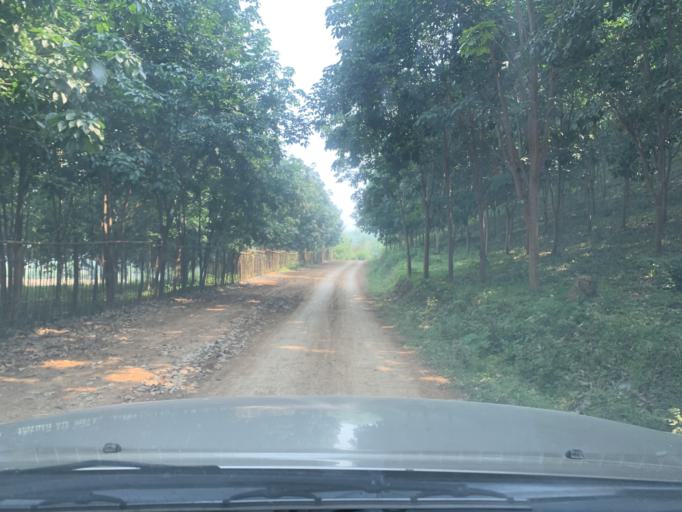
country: LA
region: Louangphabang
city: Xiang Ngeun
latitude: 19.7952
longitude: 102.1993
